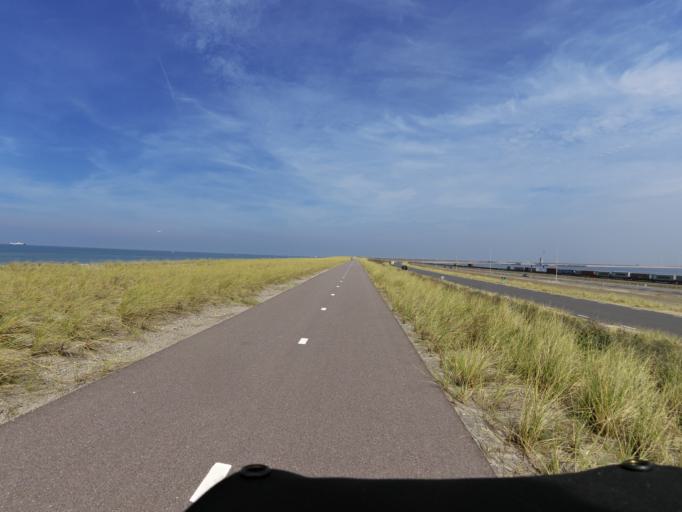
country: NL
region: South Holland
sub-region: Gemeente Goeree-Overflakkee
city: Goedereede
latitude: 51.9735
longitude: 3.9721
